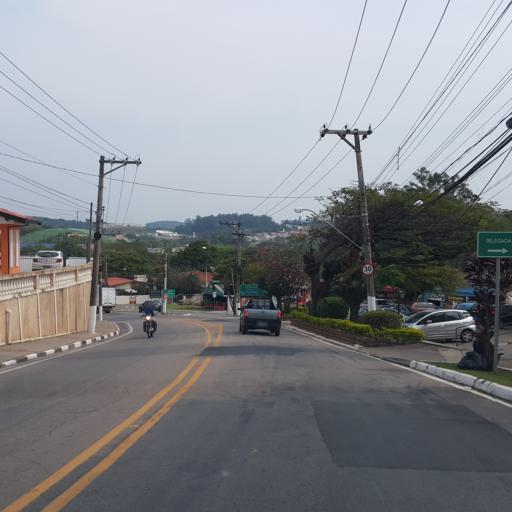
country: BR
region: Sao Paulo
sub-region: Louveira
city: Louveira
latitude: -23.0770
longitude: -46.9533
